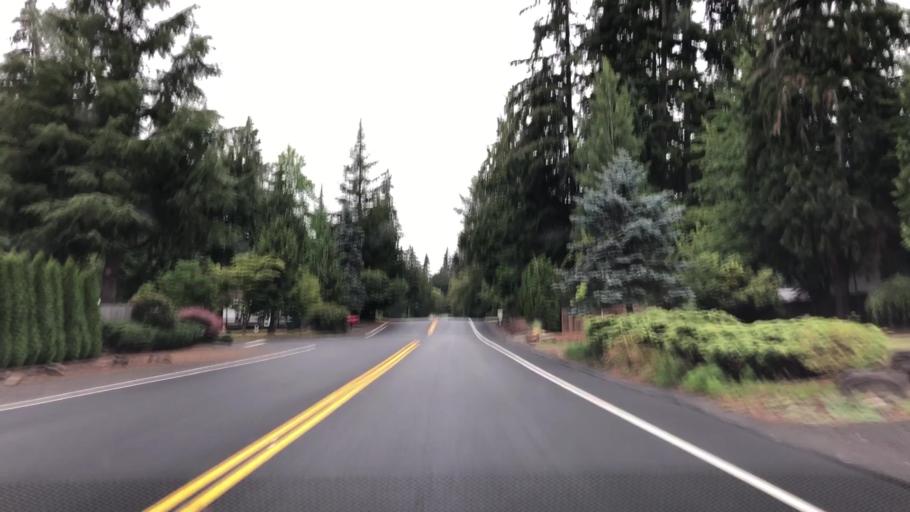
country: US
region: Washington
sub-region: Snohomish County
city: North Creek
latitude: 47.8252
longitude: -122.1995
